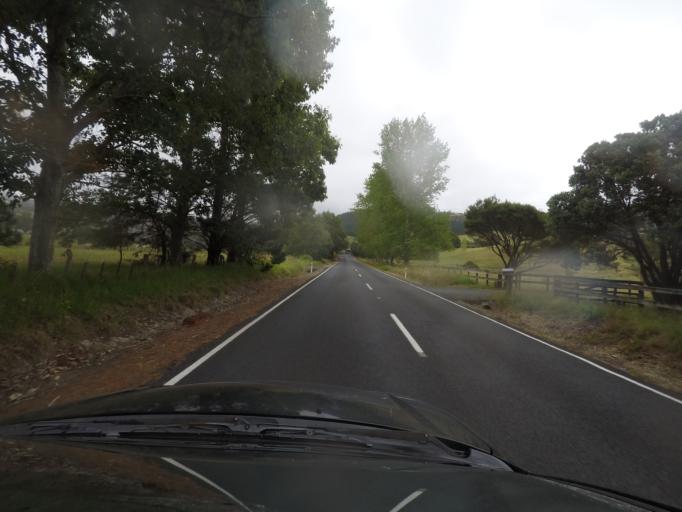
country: NZ
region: Auckland
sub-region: Auckland
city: Warkworth
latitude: -36.2648
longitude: 174.7023
